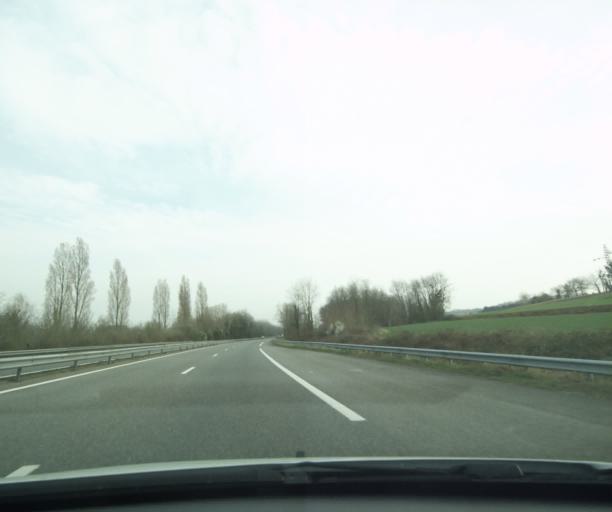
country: FR
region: Aquitaine
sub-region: Departement des Pyrenees-Atlantiques
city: Orthez
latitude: 43.5068
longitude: -0.8407
